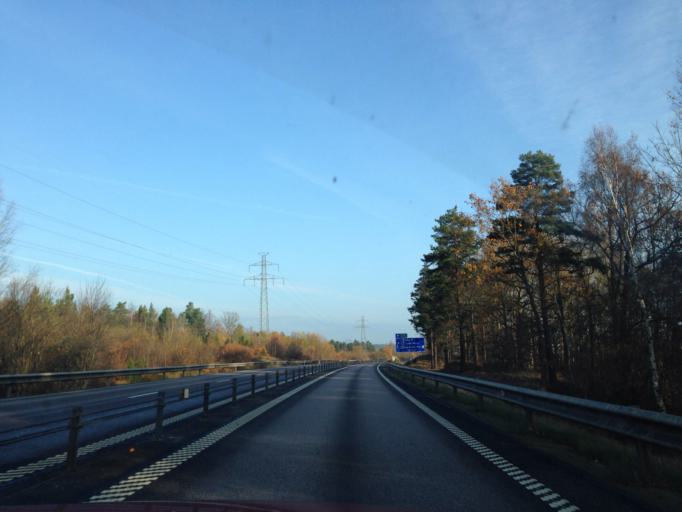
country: SE
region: Kalmar
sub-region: Oskarshamns Kommun
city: Oskarshamn
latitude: 57.2581
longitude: 16.4228
